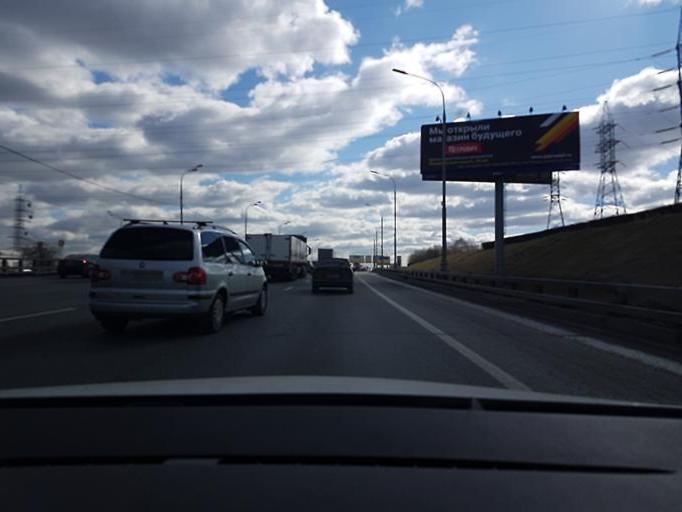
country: RU
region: Moscow
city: Strogino
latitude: 55.8377
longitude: 37.3956
